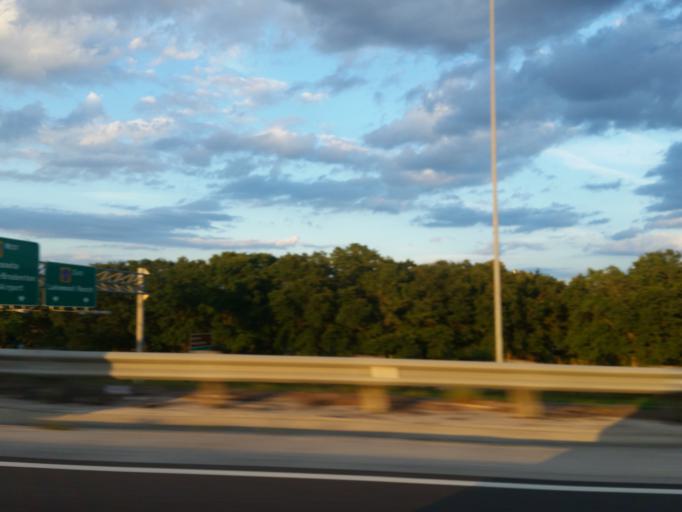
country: US
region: Florida
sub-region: Sarasota County
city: The Meadows
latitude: 27.3865
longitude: -82.4480
